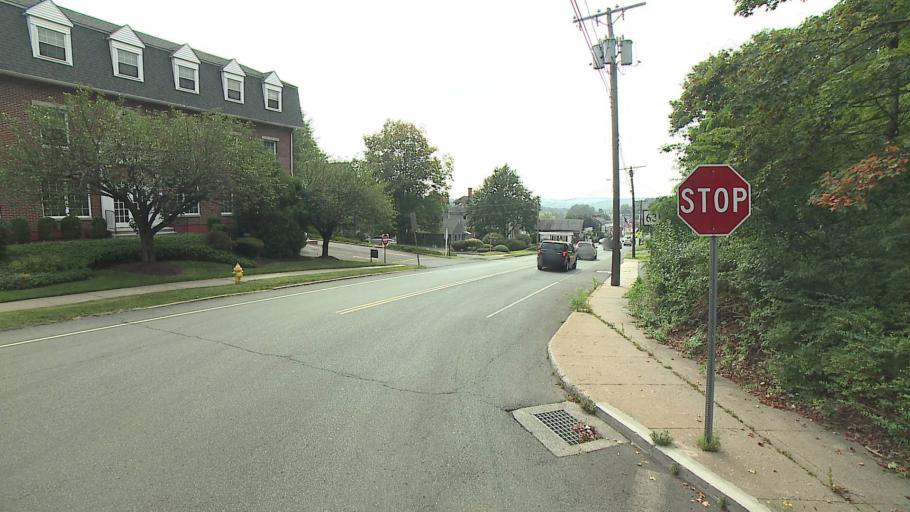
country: US
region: Connecticut
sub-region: Litchfield County
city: Watertown
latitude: 41.6051
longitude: -73.1179
